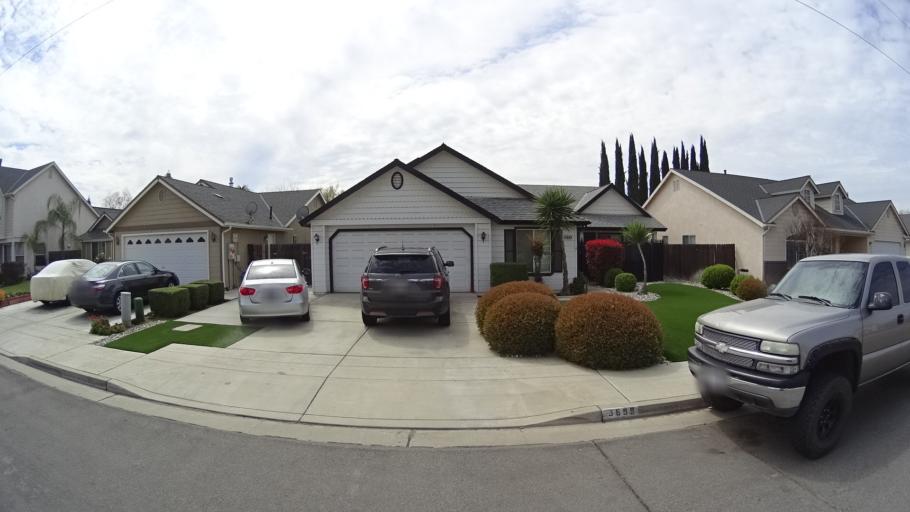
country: US
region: California
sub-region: Fresno County
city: Biola
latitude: 36.8320
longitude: -119.8937
